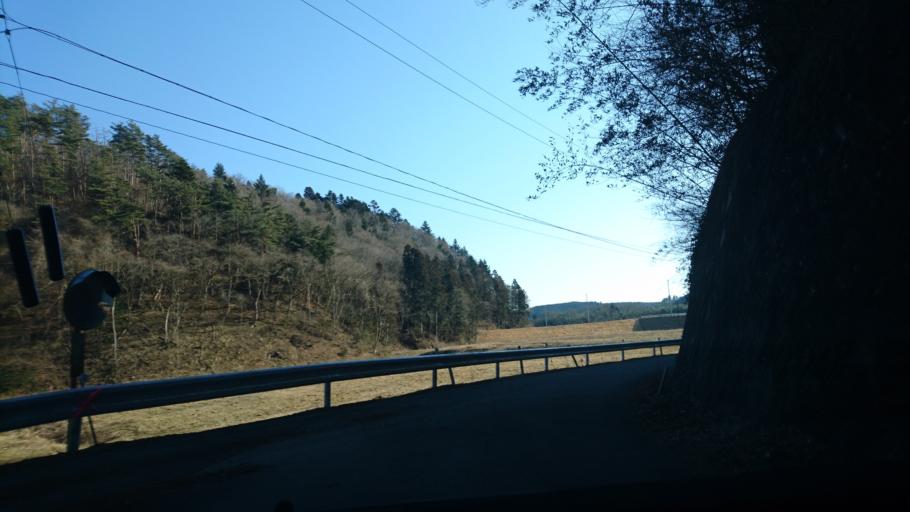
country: JP
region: Iwate
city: Ichinoseki
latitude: 38.7930
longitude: 141.2599
